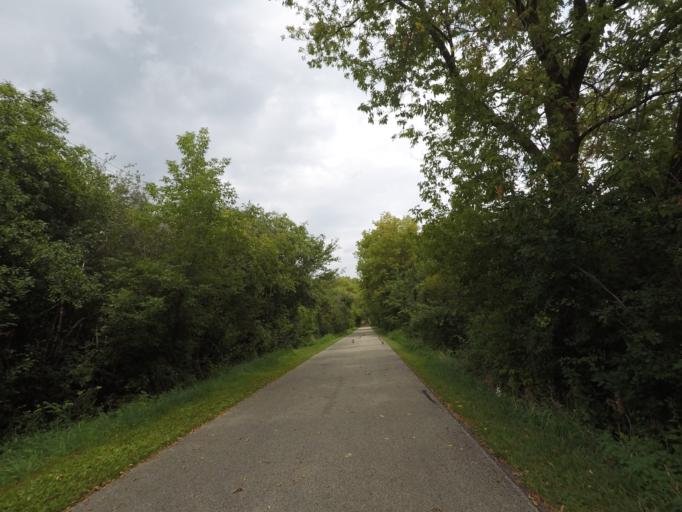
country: US
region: Wisconsin
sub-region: Jefferson County
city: Fort Atkinson
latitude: 42.9020
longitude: -88.8600
